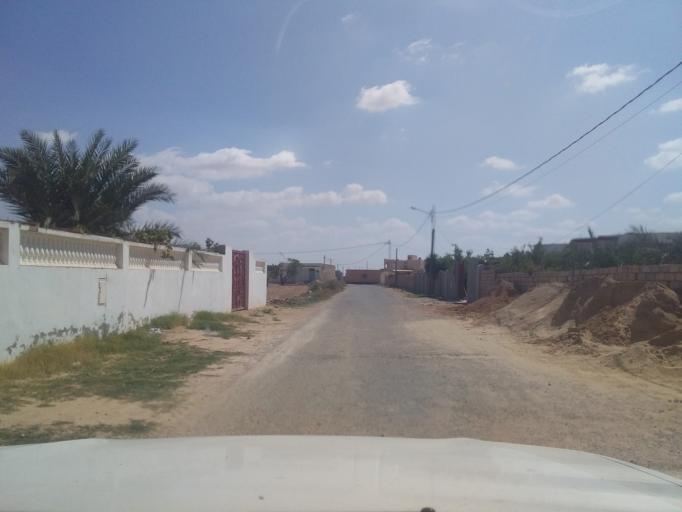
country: TN
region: Madanin
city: Medenine
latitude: 33.6127
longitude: 10.3012
